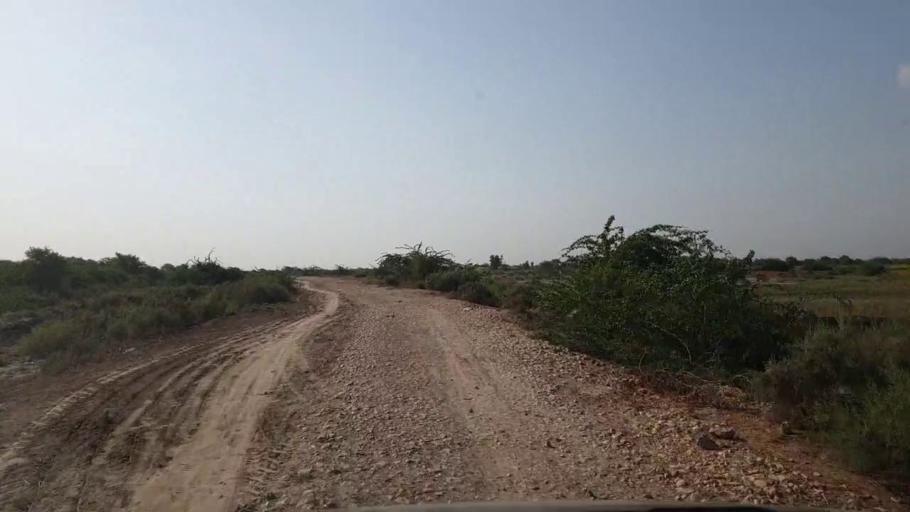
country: PK
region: Sindh
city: Kadhan
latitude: 24.6222
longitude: 69.0728
